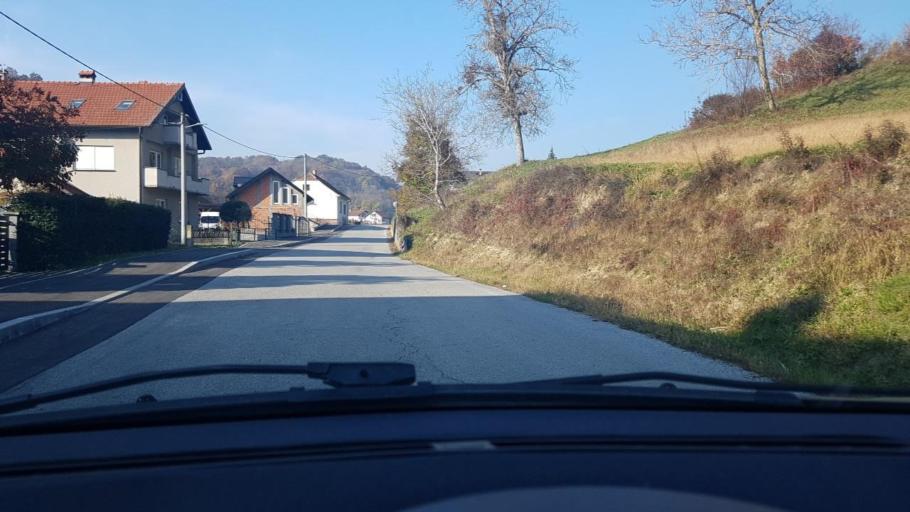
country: HR
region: Krapinsko-Zagorska
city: Zabok
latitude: 46.0240
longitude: 15.8859
